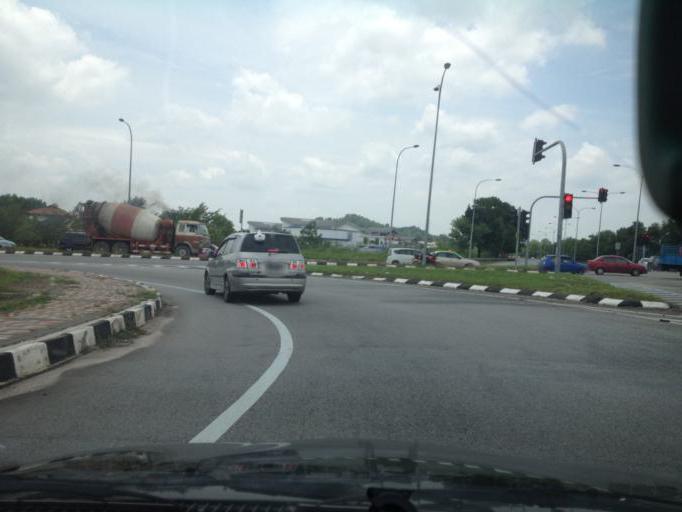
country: MY
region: Kedah
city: Sungai Petani
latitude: 5.6252
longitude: 100.5345
